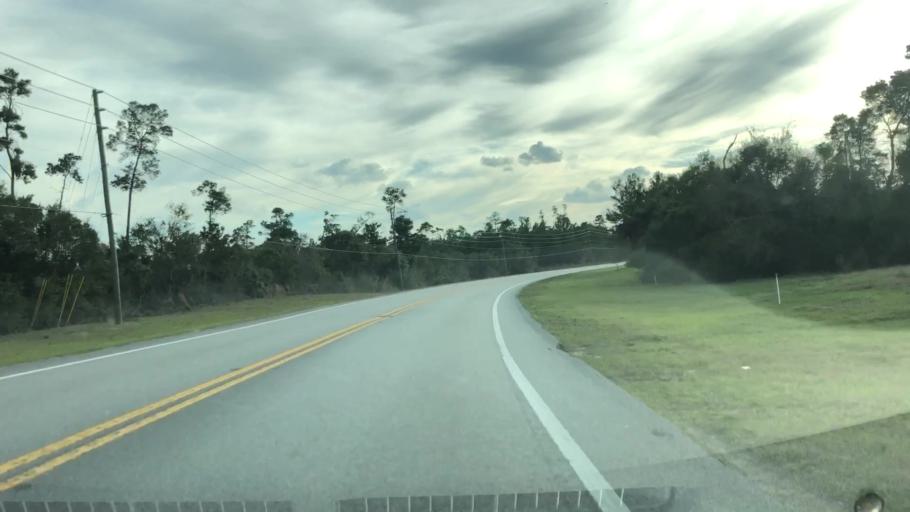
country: US
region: Florida
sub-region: Volusia County
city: Deltona
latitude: 28.9416
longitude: -81.2556
